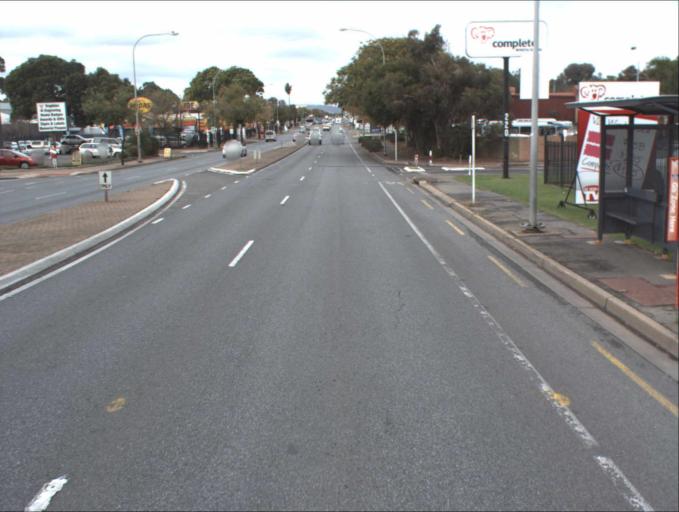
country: AU
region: South Australia
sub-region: Prospect
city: Prospect
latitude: -34.8785
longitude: 138.6025
